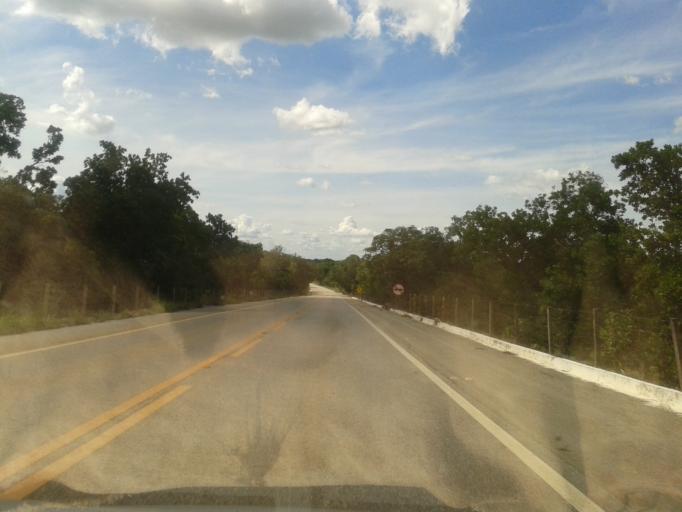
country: BR
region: Goias
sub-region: Itapuranga
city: Itapuranga
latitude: -15.4883
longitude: -50.3240
